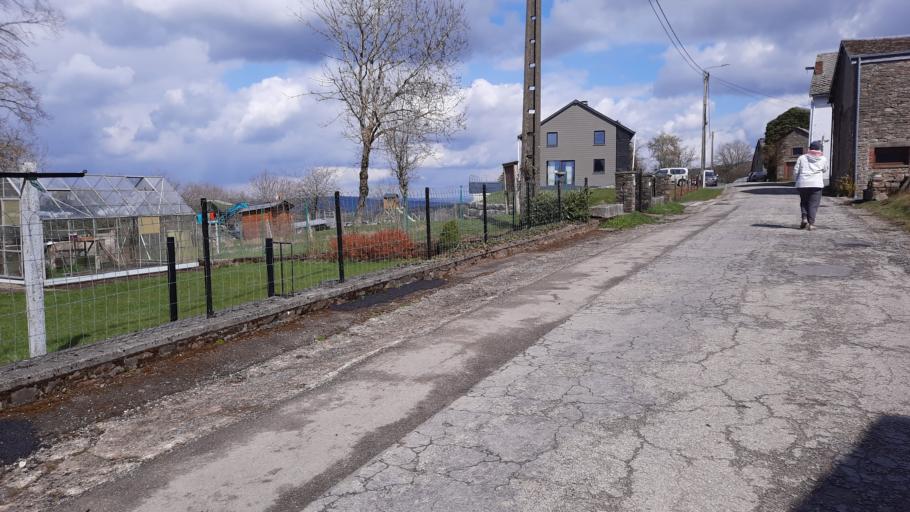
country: BE
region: Wallonia
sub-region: Province du Luxembourg
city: Manhay
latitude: 50.2808
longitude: 5.7169
